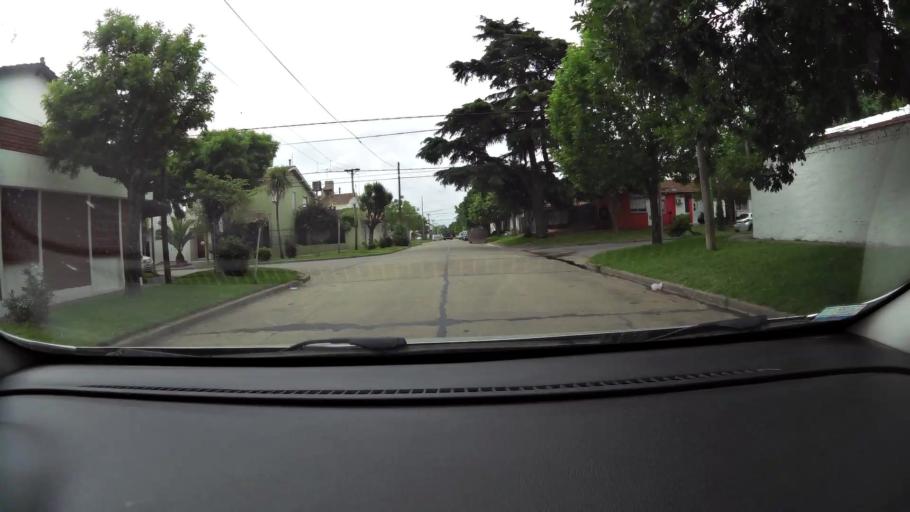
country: AR
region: Buenos Aires
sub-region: Partido de Campana
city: Campana
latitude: -34.1762
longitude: -58.9684
